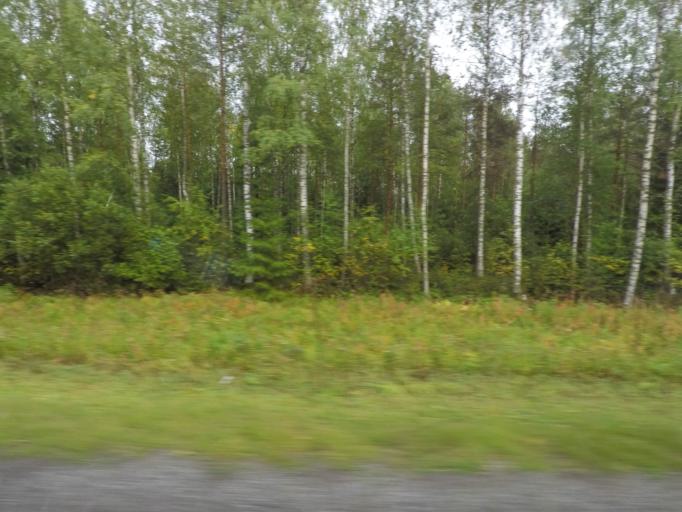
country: FI
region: Southern Savonia
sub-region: Pieksaemaeki
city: Joroinen
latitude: 62.0408
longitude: 27.8007
